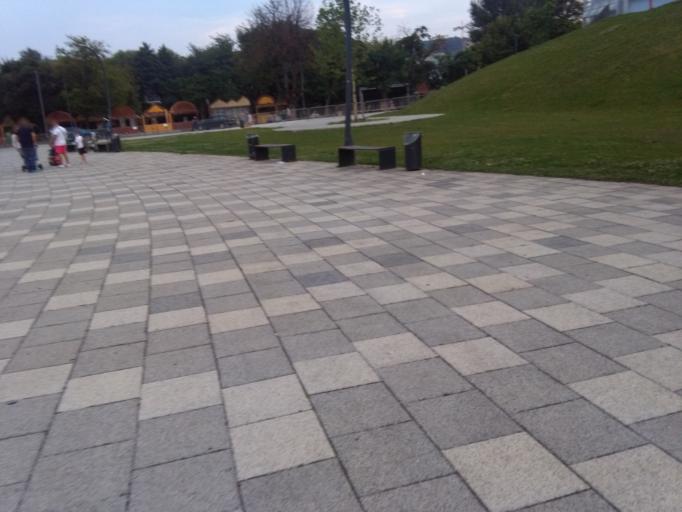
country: RO
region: Cluj
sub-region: Municipiul Cluj-Napoca
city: Cluj-Napoca
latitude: 46.7676
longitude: 23.5713
